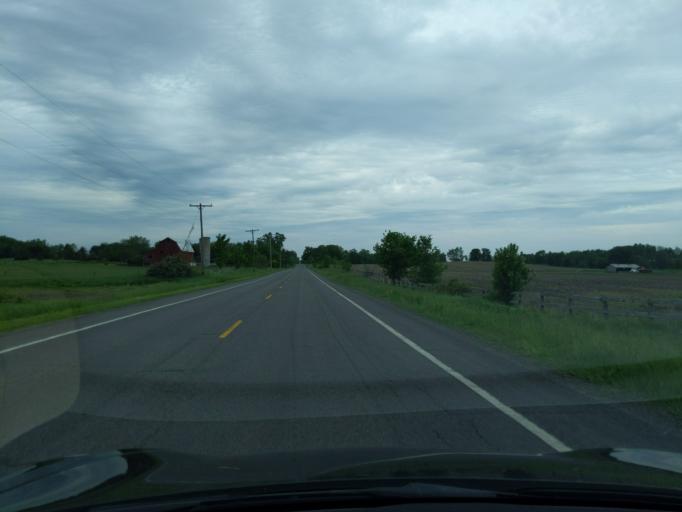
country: US
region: Michigan
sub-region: Ingham County
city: Mason
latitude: 42.5722
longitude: -84.3570
